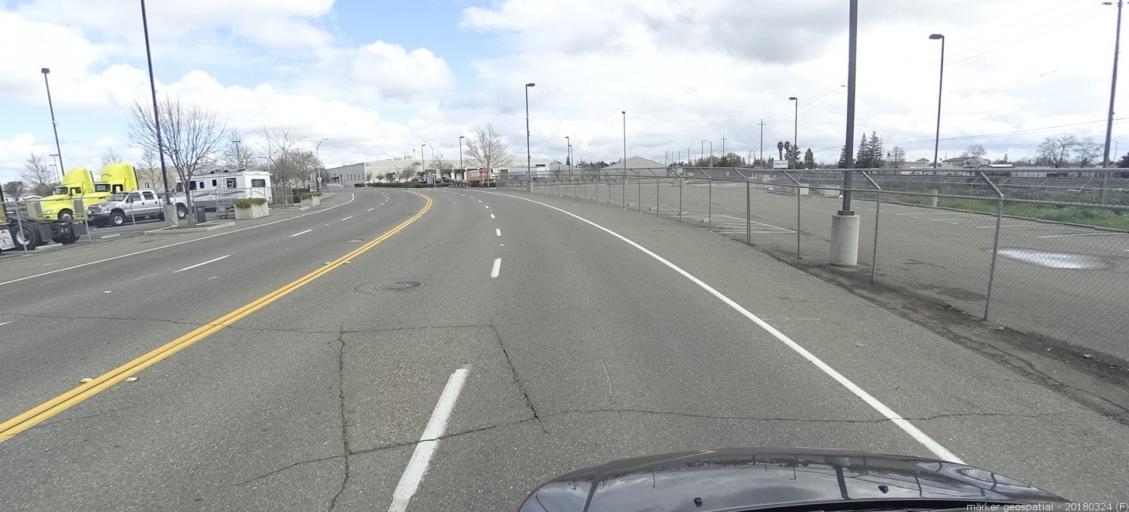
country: US
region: California
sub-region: Sacramento County
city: North Highlands
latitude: 38.6550
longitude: -121.3885
